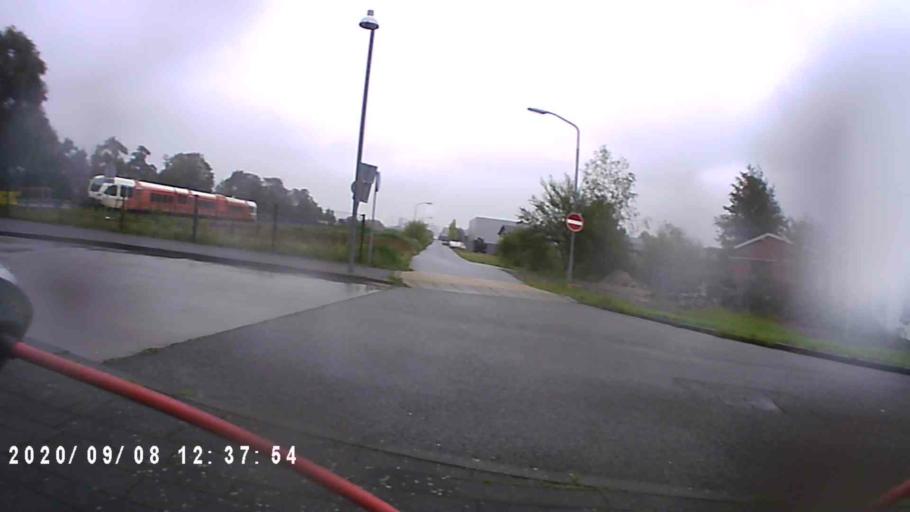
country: NL
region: Groningen
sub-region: Gemeente Veendam
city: Veendam
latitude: 53.1041
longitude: 6.8859
